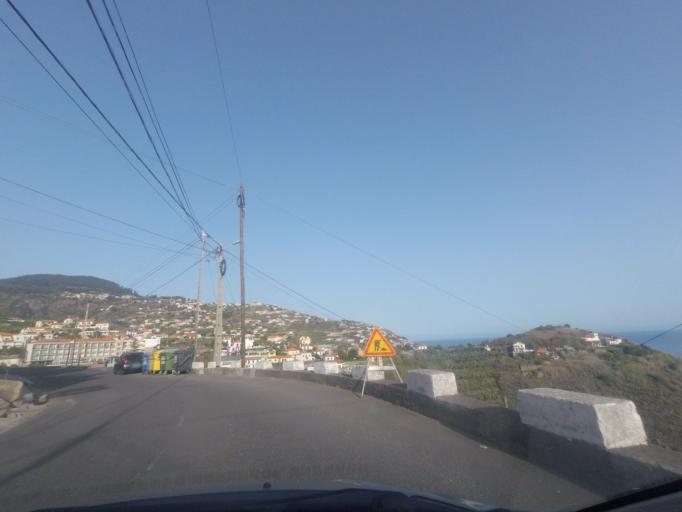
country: PT
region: Madeira
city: Ribeira Brava
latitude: 32.6767
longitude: -17.0695
